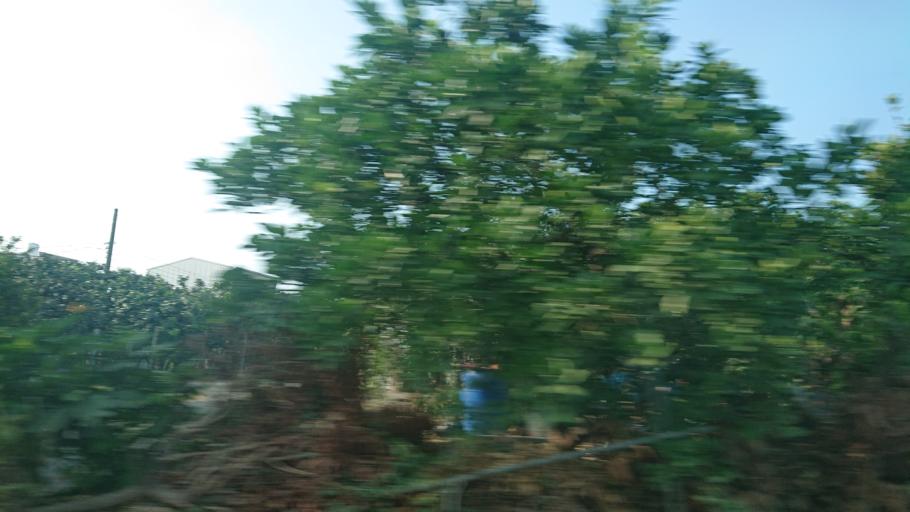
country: TW
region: Taiwan
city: Xinying
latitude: 23.1779
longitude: 120.2621
